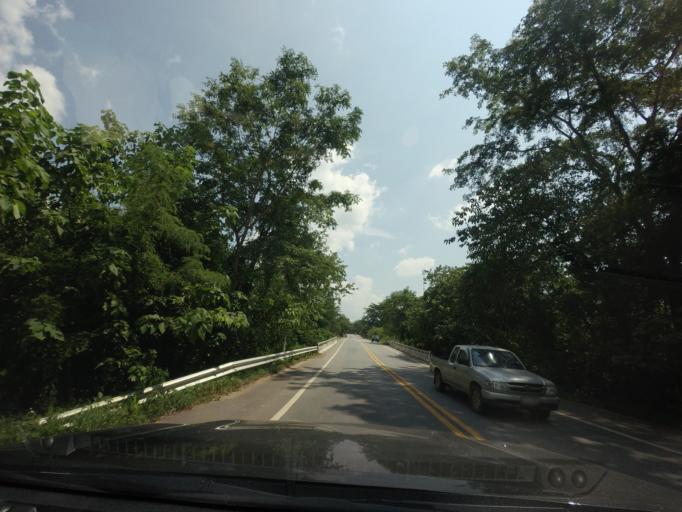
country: TH
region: Uttaradit
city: Thong Saen Khan
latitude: 17.3002
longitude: 100.4051
